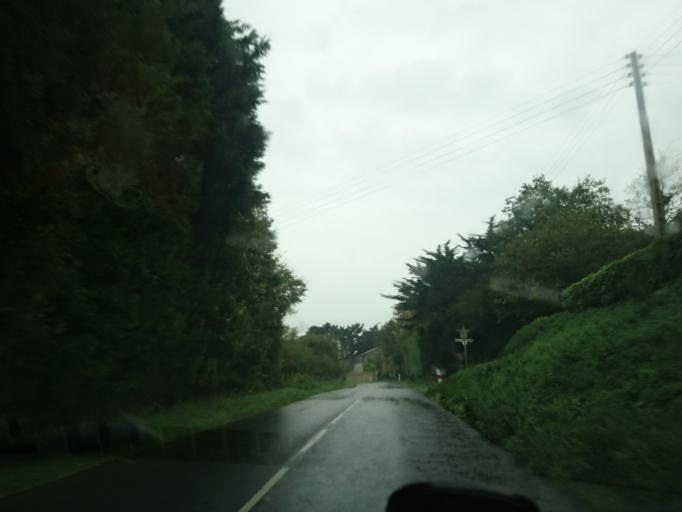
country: FR
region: Brittany
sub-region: Departement du Finistere
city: Plouguerneau
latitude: 48.5978
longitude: -4.5105
